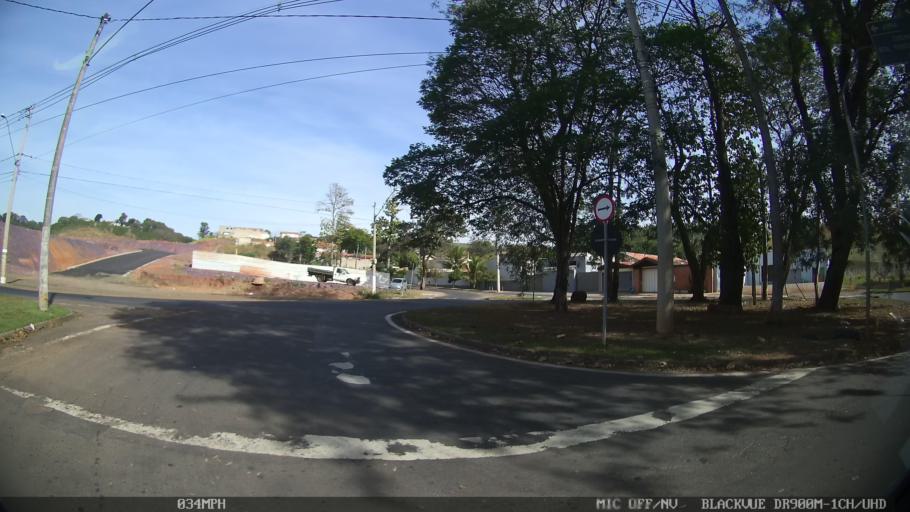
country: BR
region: Sao Paulo
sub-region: Piracicaba
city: Piracicaba
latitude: -22.7086
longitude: -47.6774
